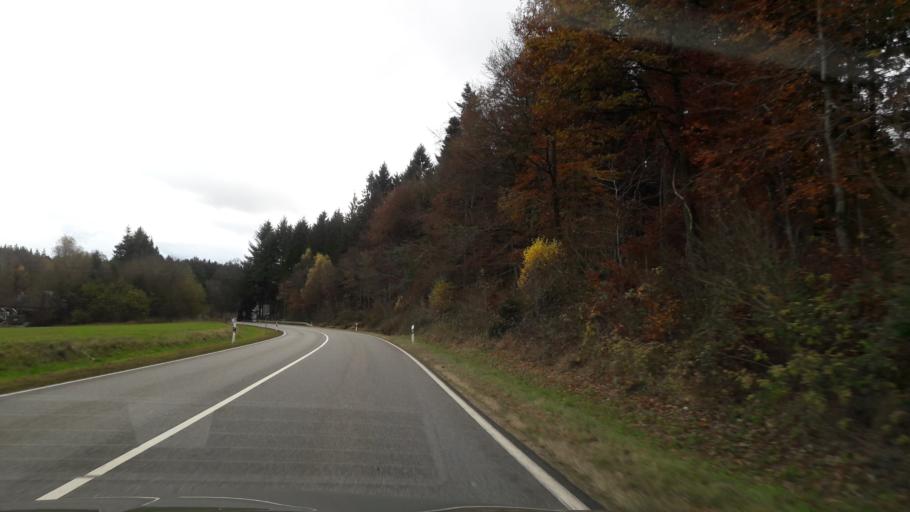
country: DE
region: Rheinland-Pfalz
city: Farschweiler
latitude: 49.7138
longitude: 6.8191
